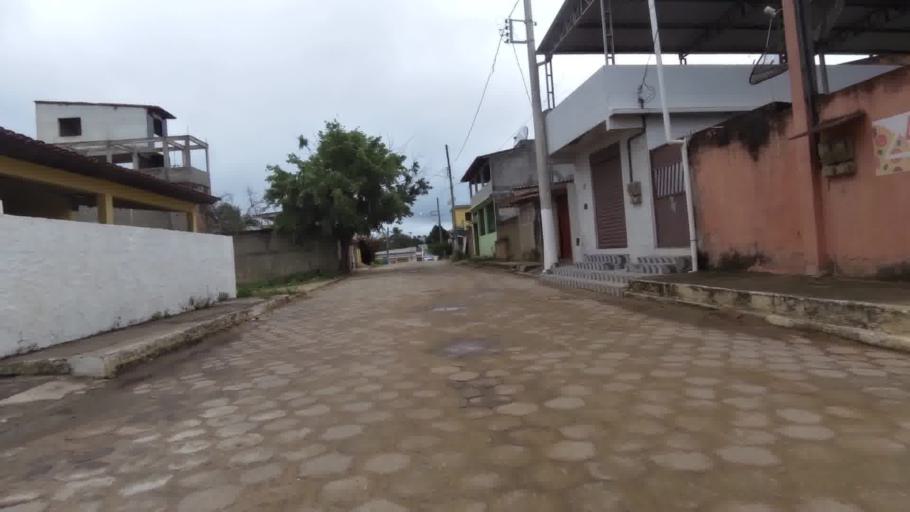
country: BR
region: Espirito Santo
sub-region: Marataizes
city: Marataizes
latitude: -21.0471
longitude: -40.8366
